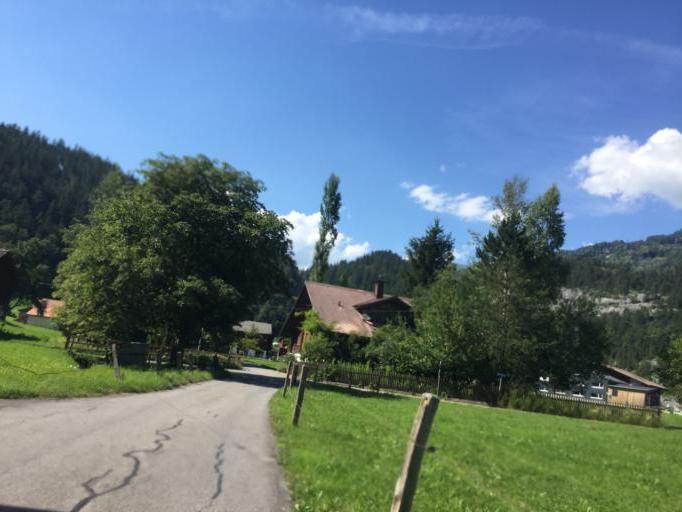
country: CH
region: Bern
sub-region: Interlaken-Oberhasli District
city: Meiringen
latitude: 46.7062
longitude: 8.2181
